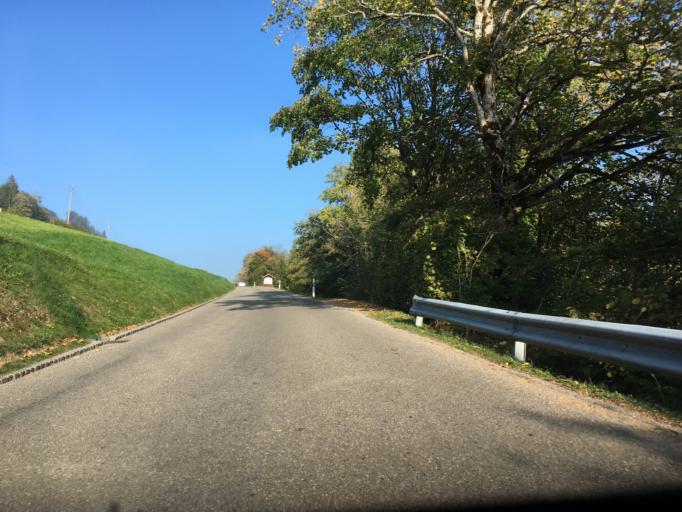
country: CH
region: Saint Gallen
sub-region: Wahlkreis Toggenburg
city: Mosnang
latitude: 47.3313
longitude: 9.0250
